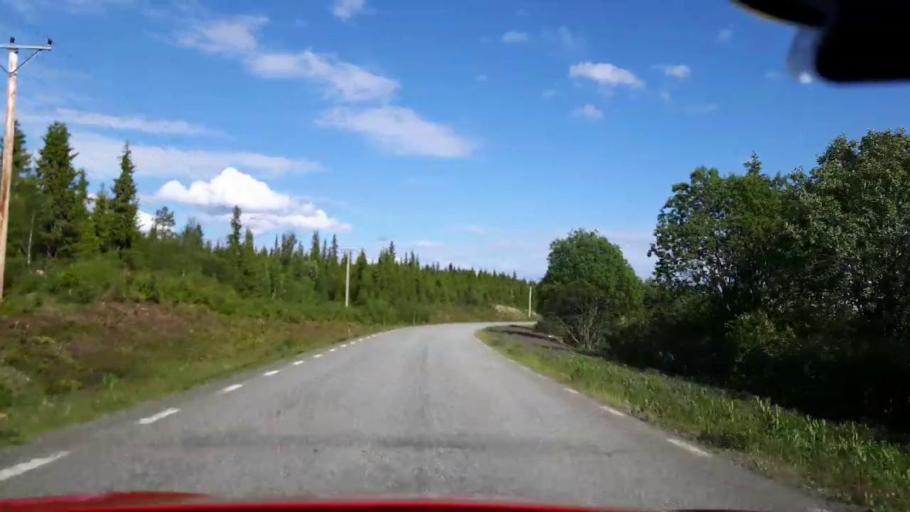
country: SE
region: Jaemtland
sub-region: Krokoms Kommun
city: Krokom
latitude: 63.6921
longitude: 14.2148
